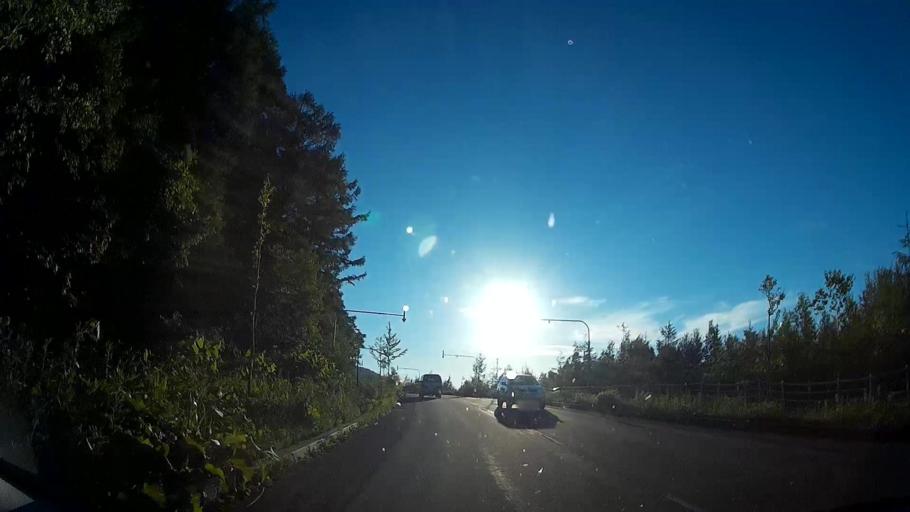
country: JP
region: Hokkaido
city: Otaru
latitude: 43.1674
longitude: 141.0206
